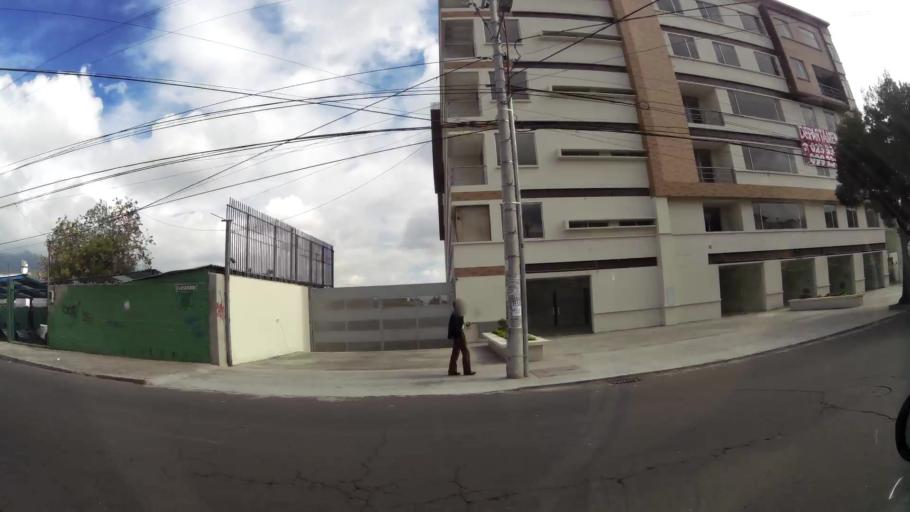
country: EC
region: Pichincha
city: Quito
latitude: -0.1566
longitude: -78.4711
